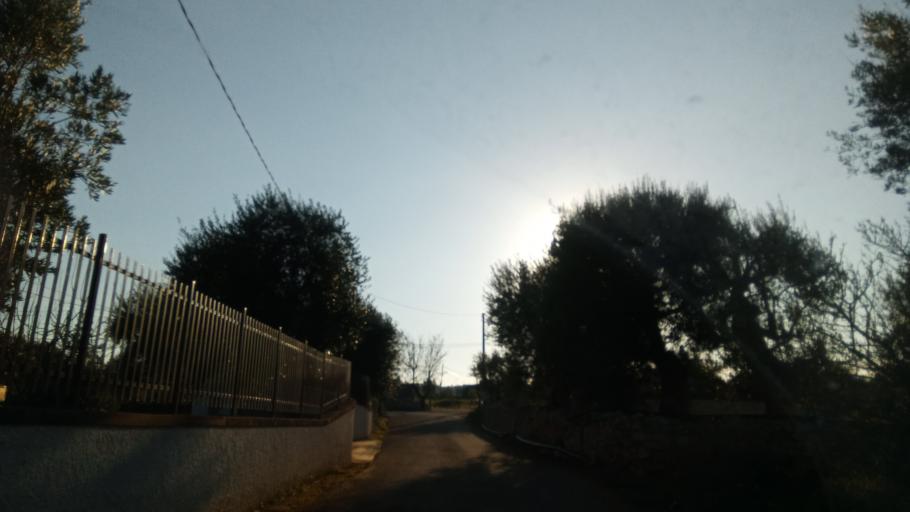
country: IT
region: Apulia
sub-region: Provincia di Bari
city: Polignano a Mare
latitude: 40.9808
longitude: 17.2080
